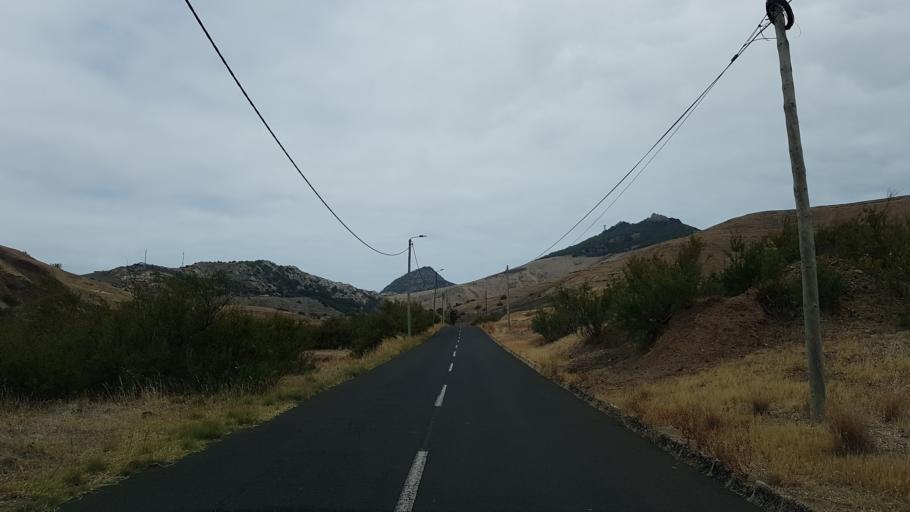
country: PT
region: Madeira
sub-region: Porto Santo
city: Vila de Porto Santo
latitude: 33.0708
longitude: -16.3009
